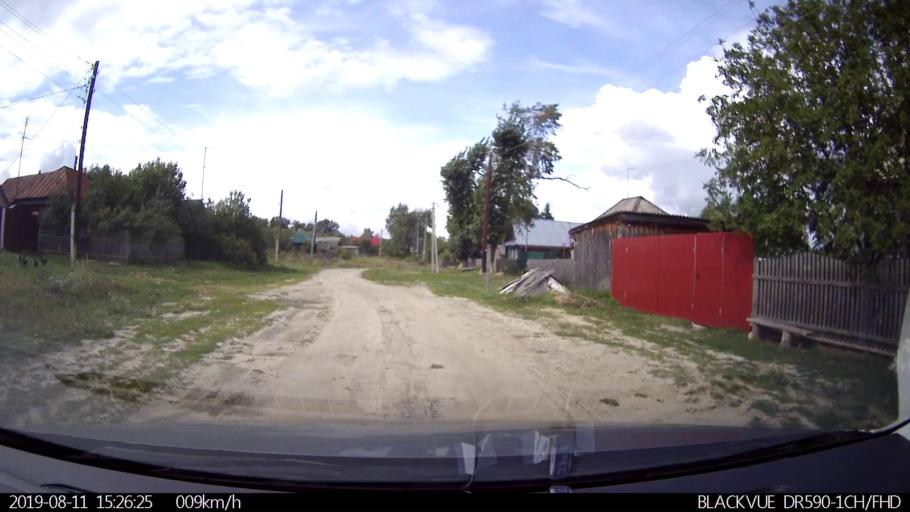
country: RU
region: Ulyanovsk
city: Ignatovka
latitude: 53.8501
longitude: 47.5761
